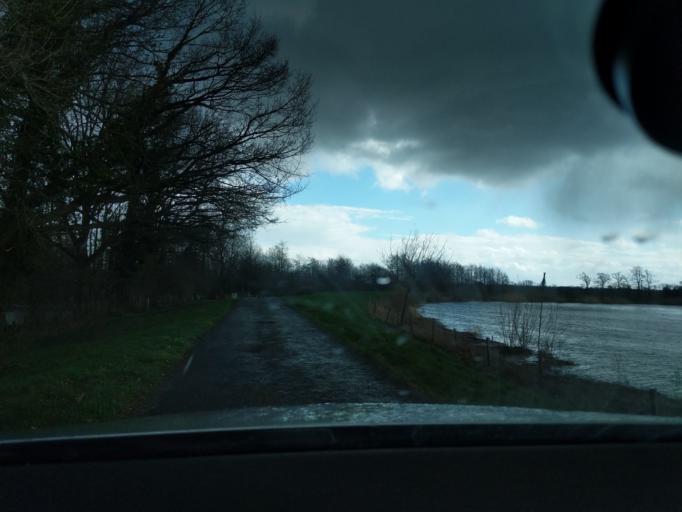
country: DE
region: Lower Saxony
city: Kranenburg
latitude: 53.6237
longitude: 9.2031
